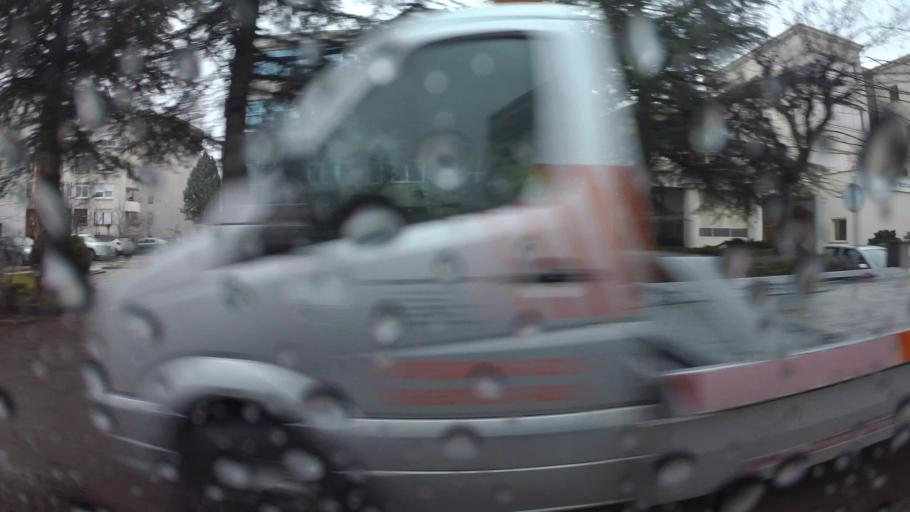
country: BA
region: Federation of Bosnia and Herzegovina
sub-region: Hercegovacko-Bosanski Kanton
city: Mostar
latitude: 43.3503
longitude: 17.7969
